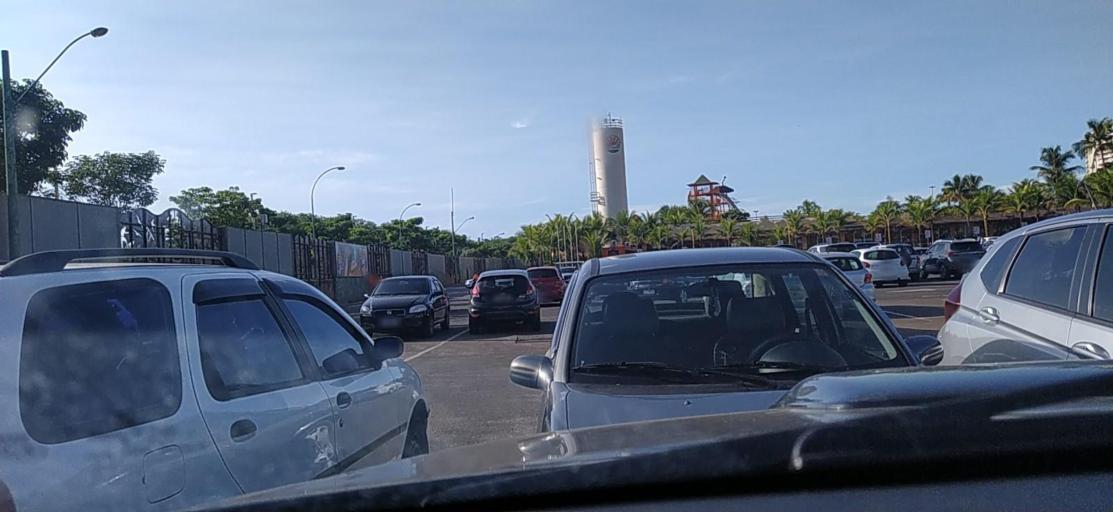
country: BR
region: Sao Paulo
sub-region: Olimpia
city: Olimpia
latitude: -20.7233
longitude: -48.9182
